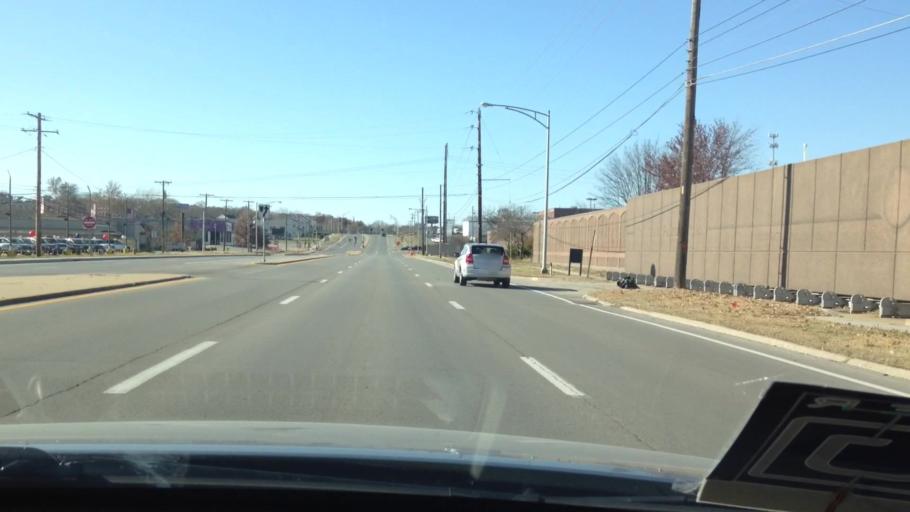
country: US
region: Kansas
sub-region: Johnson County
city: Leawood
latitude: 38.9553
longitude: -94.5743
